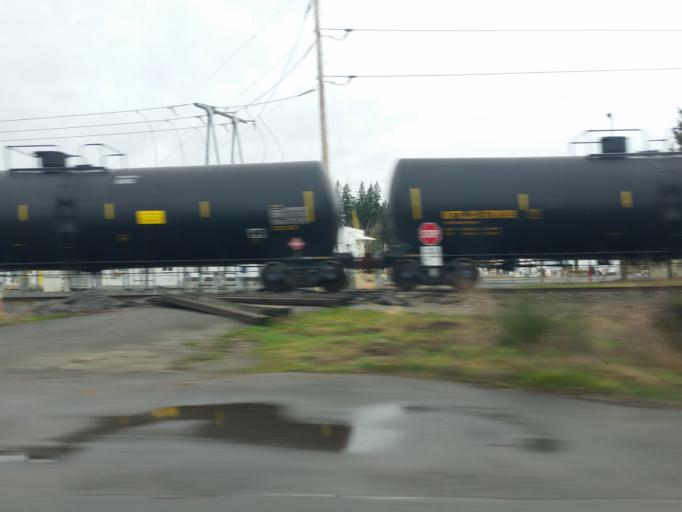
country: US
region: Washington
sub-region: Skagit County
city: Mount Vernon
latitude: 48.4552
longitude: -122.3895
